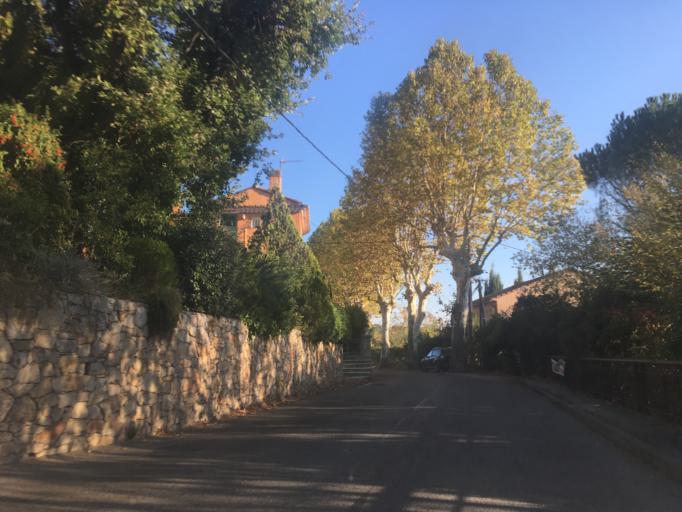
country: FR
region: Provence-Alpes-Cote d'Azur
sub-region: Departement du Var
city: Villecroze
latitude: 43.5820
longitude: 6.2773
